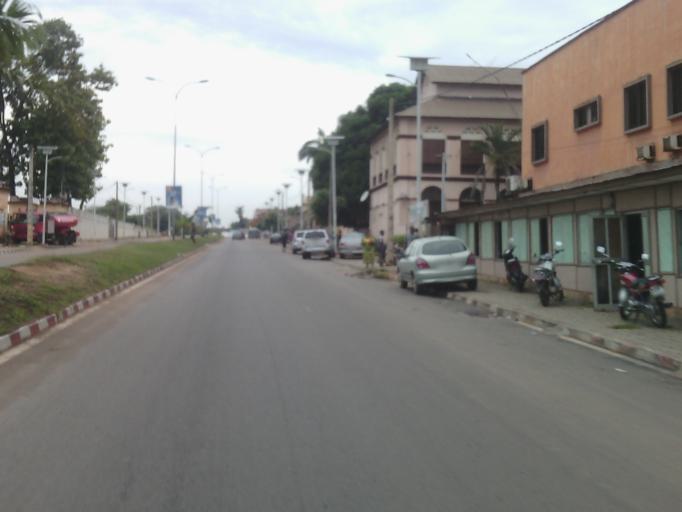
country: BJ
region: Queme
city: Porto-Novo
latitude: 6.4706
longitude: 2.6200
